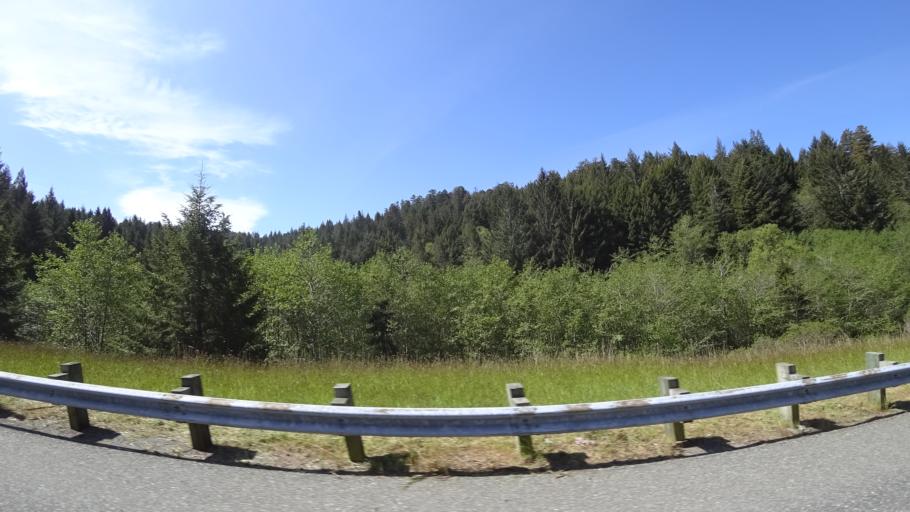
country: US
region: California
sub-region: Del Norte County
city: Bertsch-Oceanview
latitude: 41.4537
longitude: -124.0300
